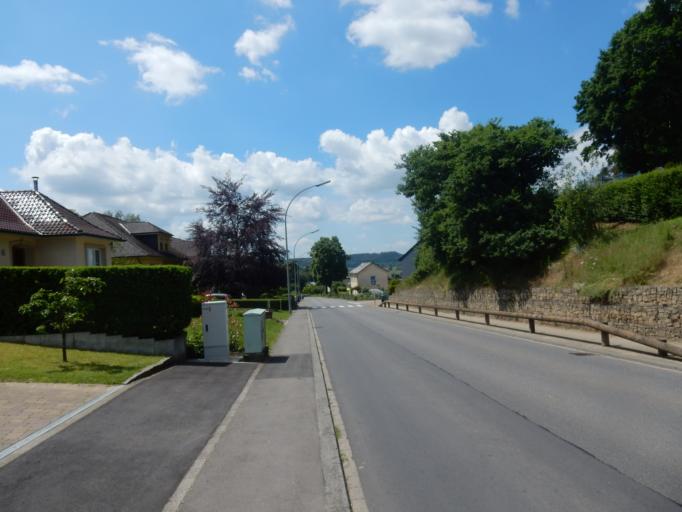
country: LU
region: Luxembourg
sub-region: Canton de Mersch
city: Tuntange
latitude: 49.7374
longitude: 6.0273
